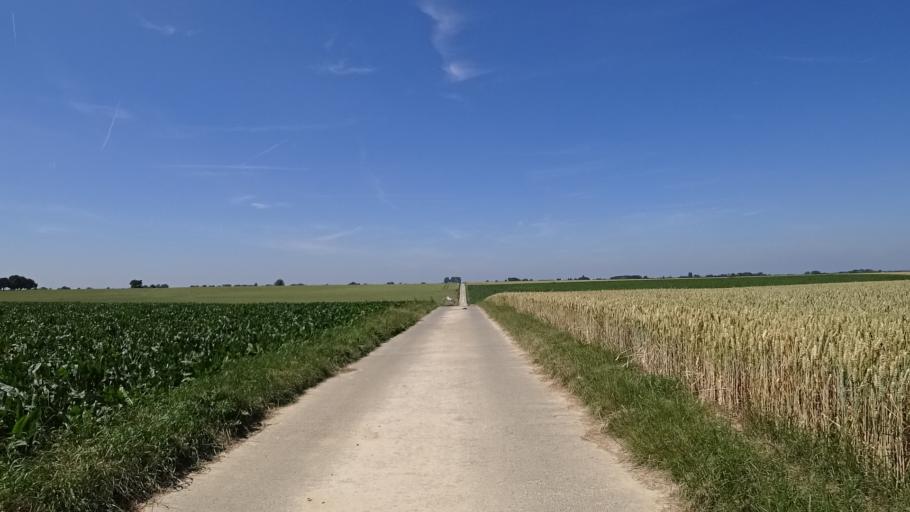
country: BE
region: Wallonia
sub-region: Province du Brabant Wallon
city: Perwez
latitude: 50.6596
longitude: 4.8430
